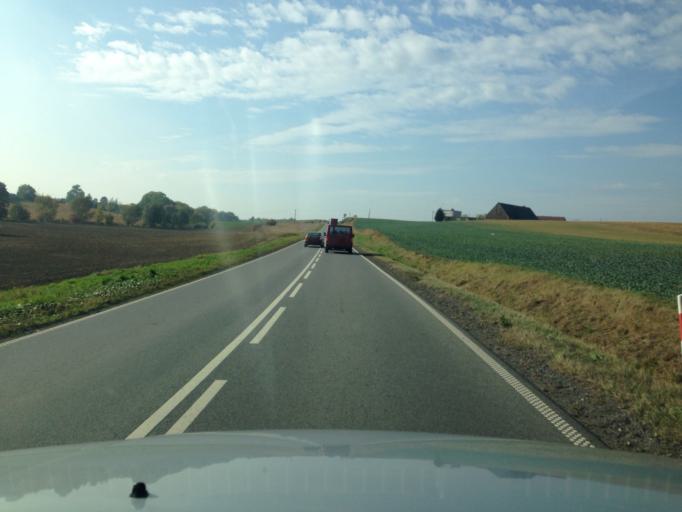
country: PL
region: Kujawsko-Pomorskie
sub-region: Powiat grudziadzki
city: Gruta
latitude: 53.4398
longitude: 18.8762
